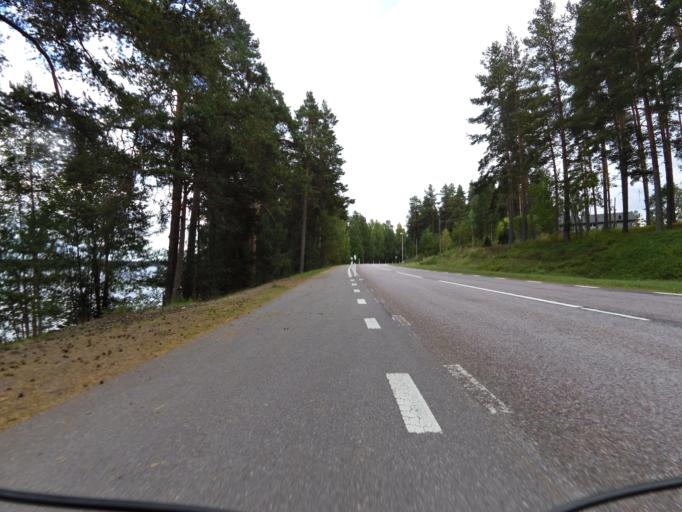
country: SE
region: Gaevleborg
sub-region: Sandvikens Kommun
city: Sandviken
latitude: 60.7018
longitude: 16.8147
